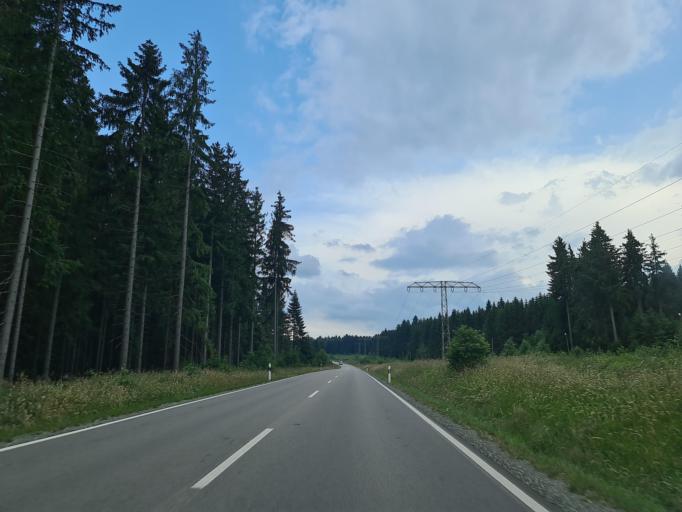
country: DE
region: Saxony
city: Grunbach
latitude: 50.4342
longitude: 12.3674
